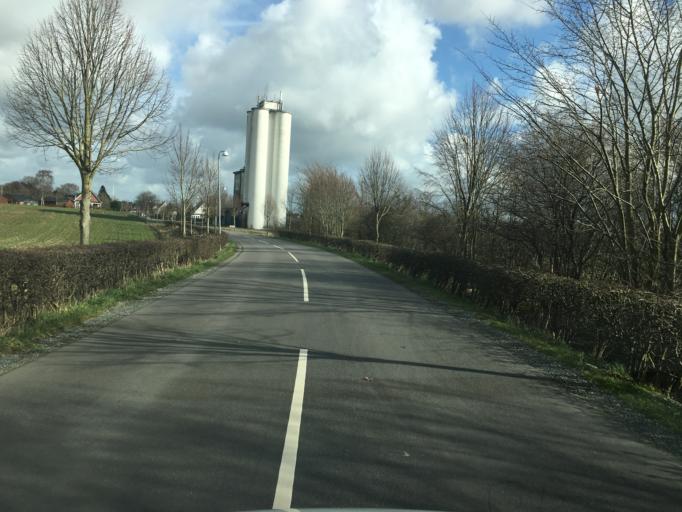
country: DK
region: South Denmark
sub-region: Aabenraa Kommune
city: Krusa
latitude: 54.8968
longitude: 9.4380
